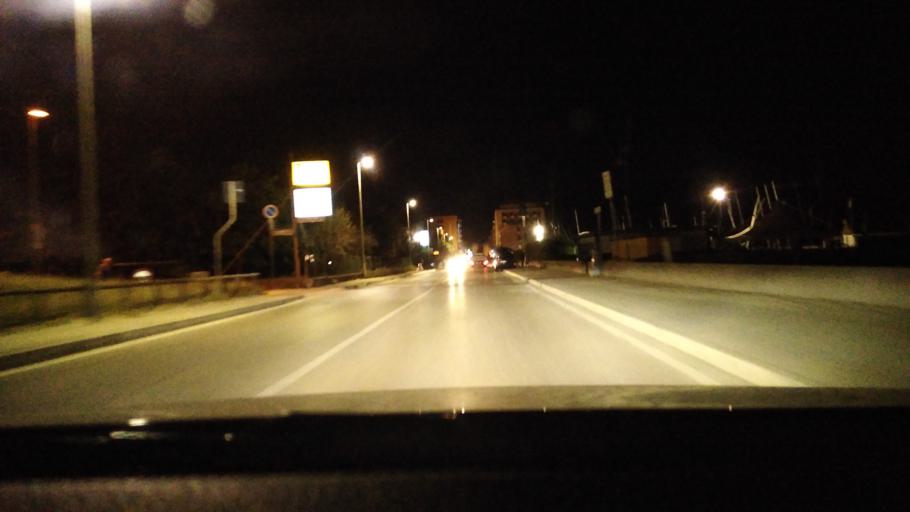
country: IT
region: Emilia-Romagna
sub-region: Provincia di Rimini
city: Bellaria-Igea Marina
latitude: 44.1273
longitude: 12.4898
